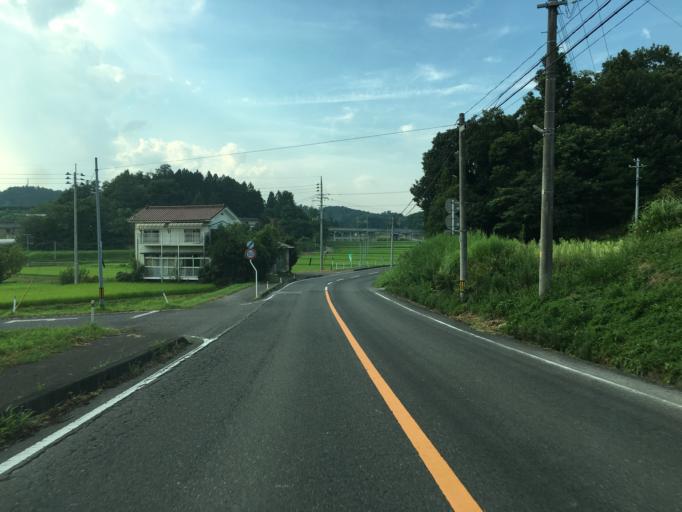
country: JP
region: Fukushima
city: Motomiya
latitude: 37.5296
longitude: 140.4432
